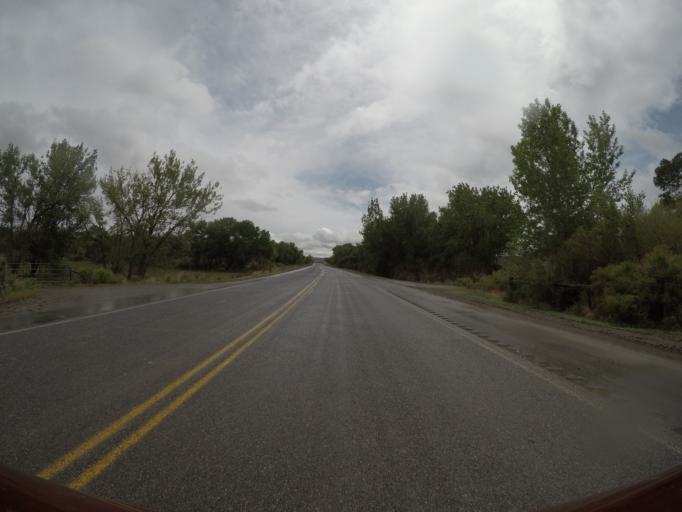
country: US
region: Wyoming
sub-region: Big Horn County
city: Lovell
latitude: 44.8634
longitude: -108.3316
